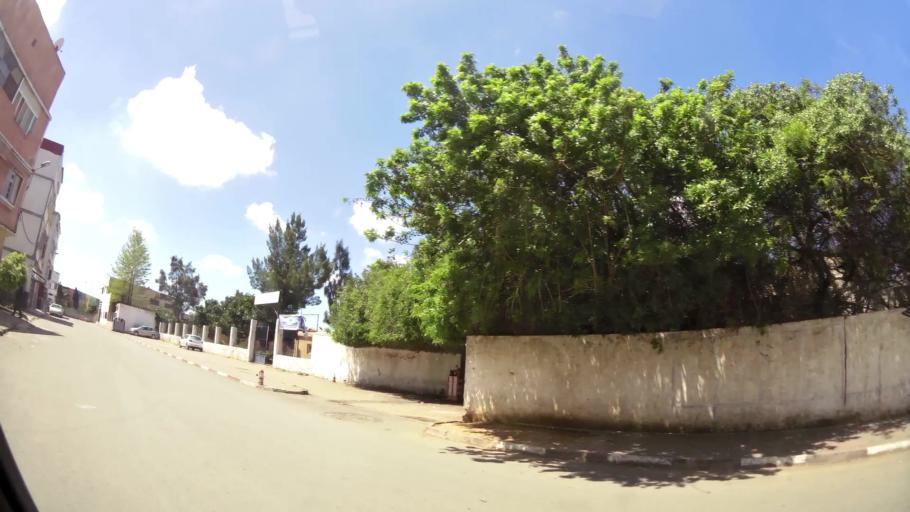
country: MA
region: Grand Casablanca
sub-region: Casablanca
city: Casablanca
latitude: 33.5591
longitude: -7.5864
